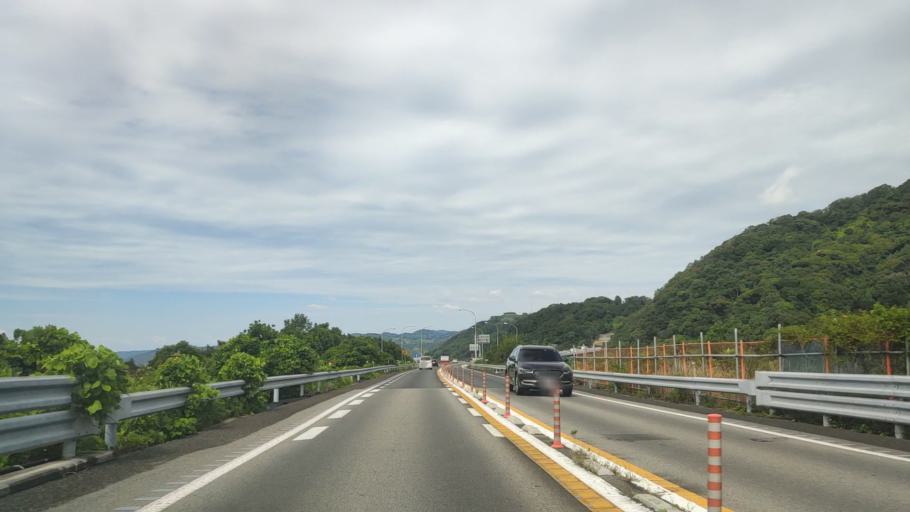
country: JP
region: Wakayama
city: Gobo
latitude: 34.0092
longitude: 135.1911
